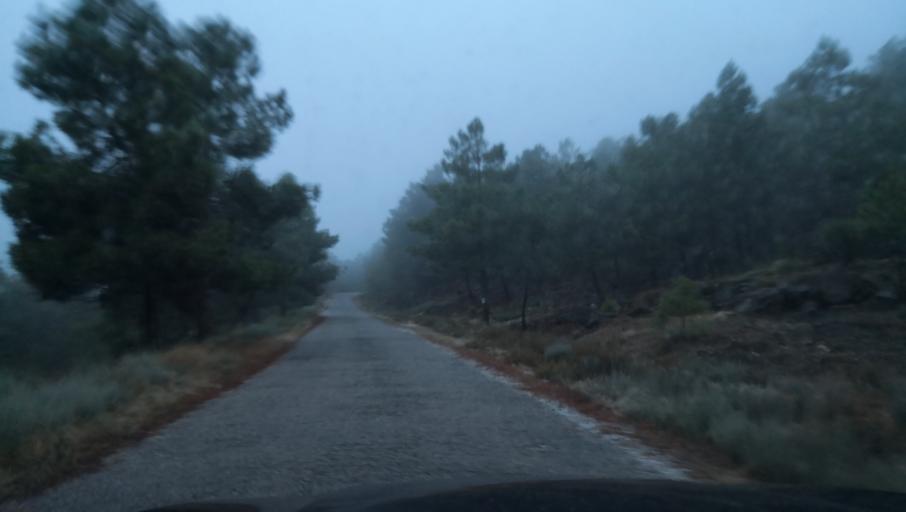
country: PT
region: Vila Real
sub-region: Sabrosa
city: Sabrosa
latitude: 41.2822
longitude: -7.5893
